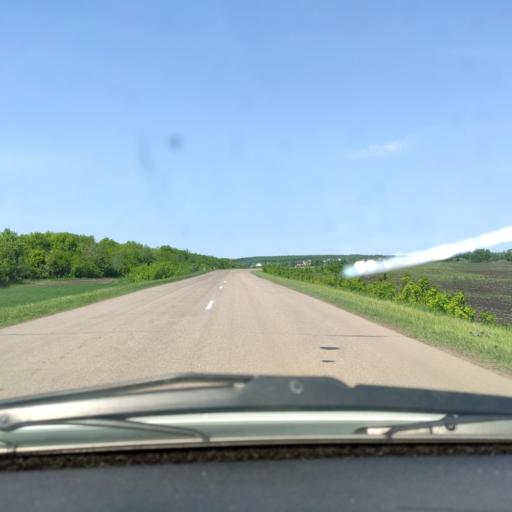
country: RU
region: Bashkortostan
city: Avdon
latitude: 54.5412
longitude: 55.6467
